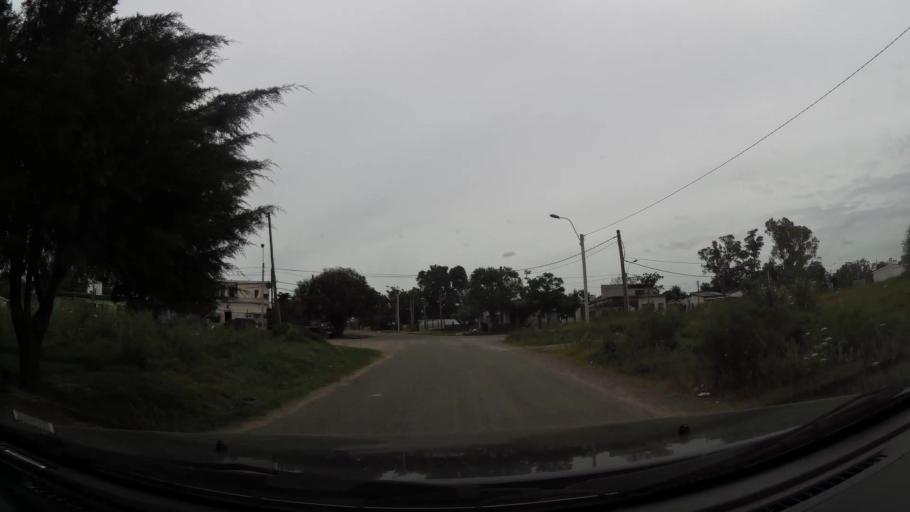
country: UY
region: Canelones
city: Las Piedras
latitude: -34.7307
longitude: -56.2062
